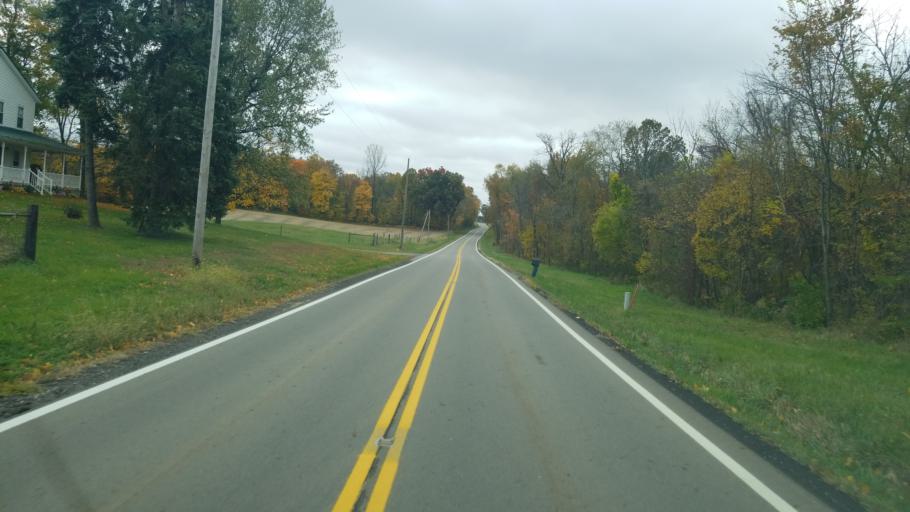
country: US
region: Ohio
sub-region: Richland County
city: Shelby
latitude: 40.9188
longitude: -82.7331
